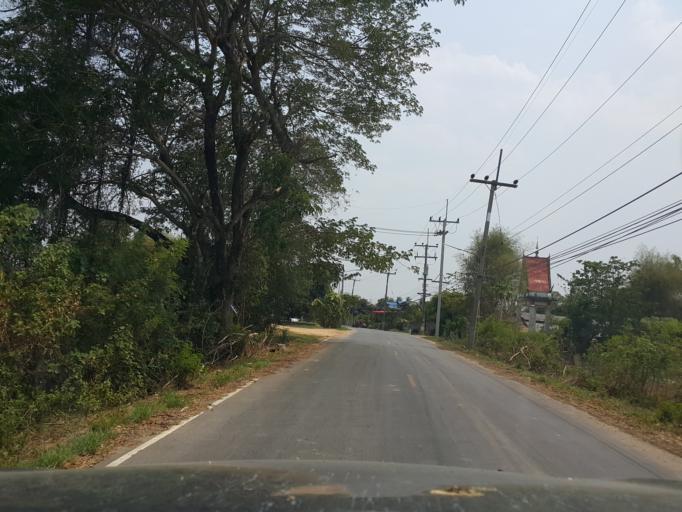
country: TH
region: Lampang
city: Mae Phrik
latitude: 17.5026
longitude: 99.1289
